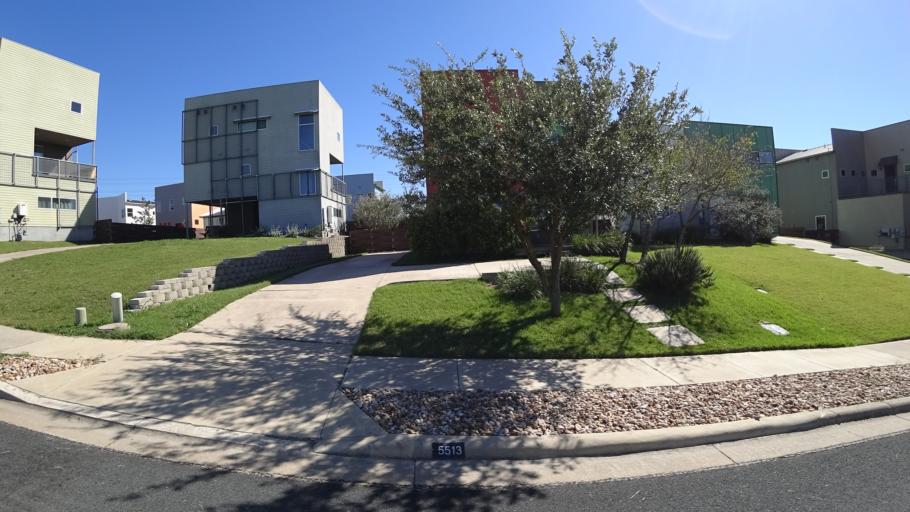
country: US
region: Texas
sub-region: Travis County
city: Hornsby Bend
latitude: 30.2860
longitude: -97.6461
